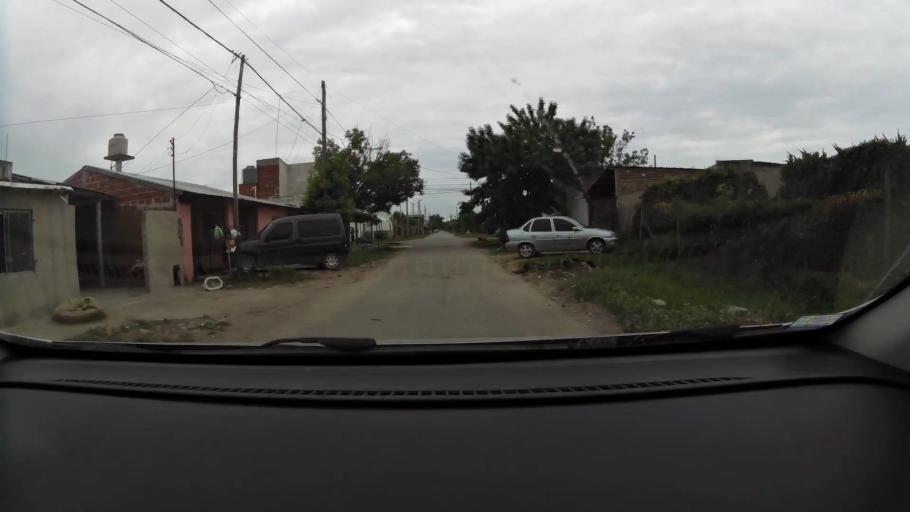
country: AR
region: Buenos Aires
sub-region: Partido de Zarate
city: Zarate
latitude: -34.1154
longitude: -59.0319
